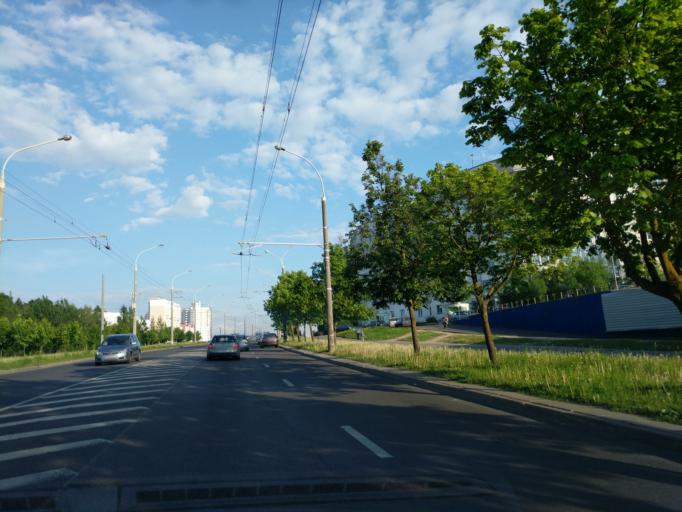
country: BY
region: Minsk
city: Novoye Medvezhino
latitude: 53.8917
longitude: 27.4384
